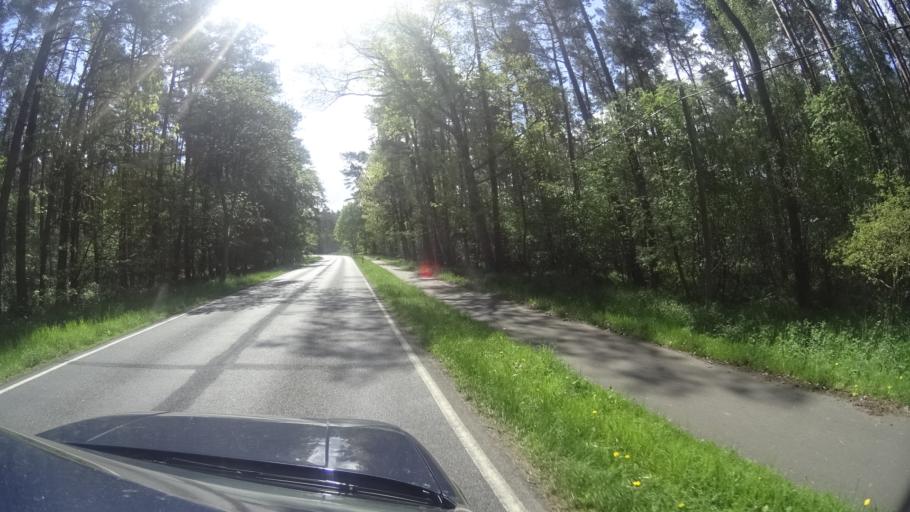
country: DE
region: Mecklenburg-Vorpommern
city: Barth
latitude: 54.3644
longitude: 12.6410
